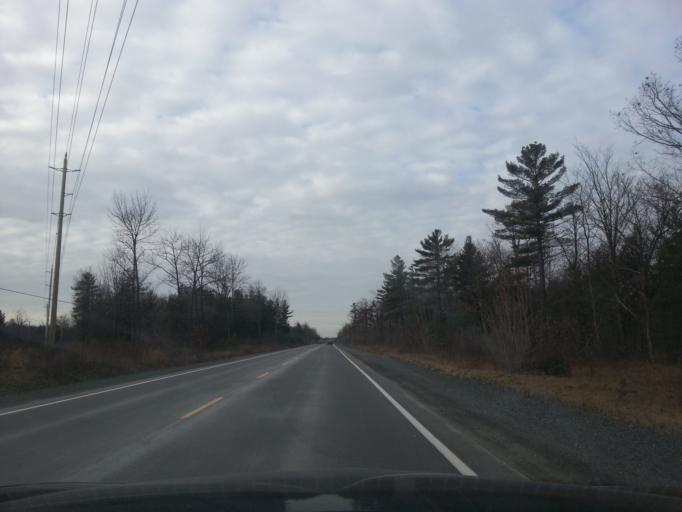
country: CA
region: Ontario
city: Quinte West
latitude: 44.4677
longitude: -77.7204
